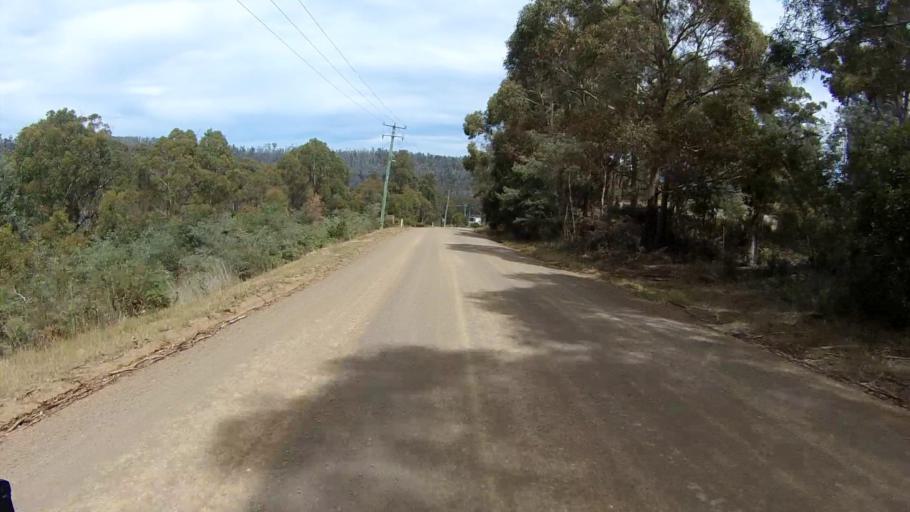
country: AU
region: Tasmania
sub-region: Sorell
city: Sorell
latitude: -42.8021
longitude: 147.6754
